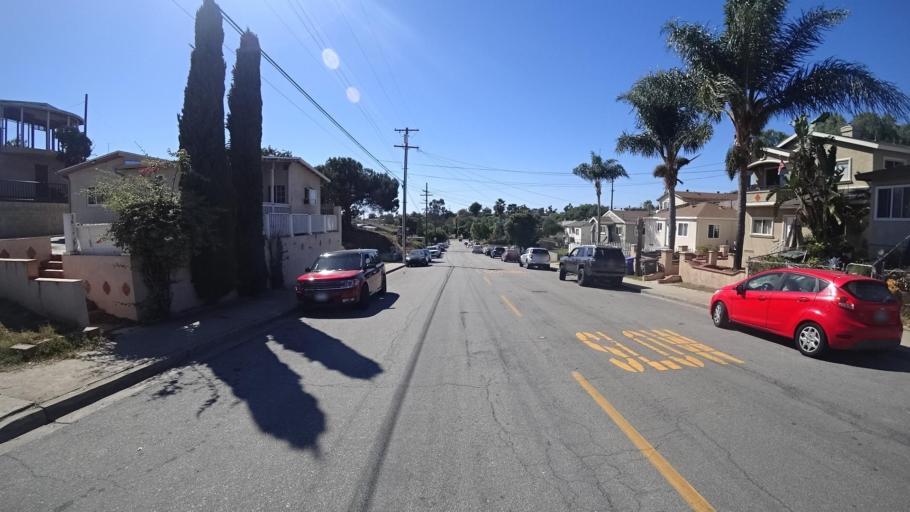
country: US
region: California
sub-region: San Diego County
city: National City
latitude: 32.6697
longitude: -117.0742
